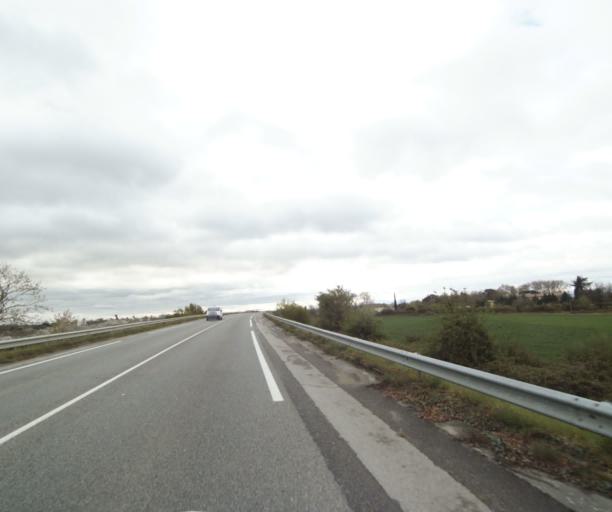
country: FR
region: Midi-Pyrenees
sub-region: Departement de l'Ariege
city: Saverdun
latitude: 43.2331
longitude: 1.6006
